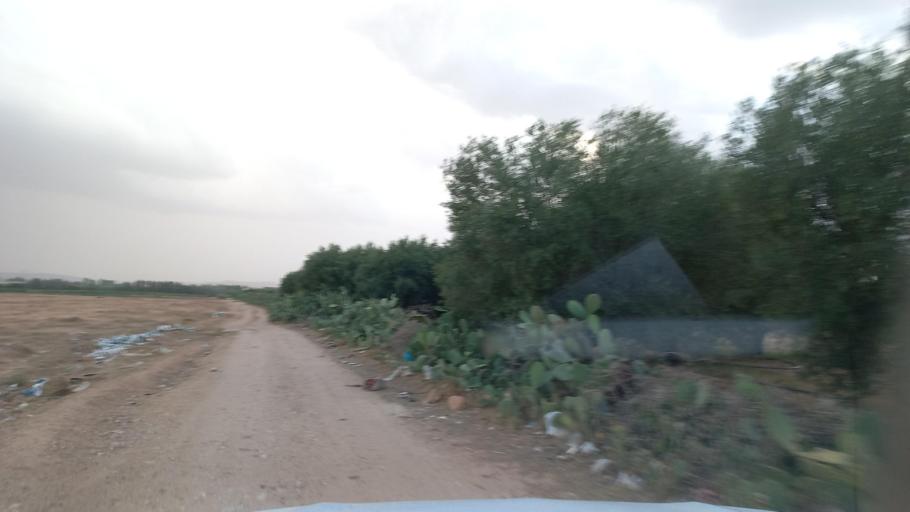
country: TN
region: Al Qasrayn
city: Kasserine
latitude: 35.2780
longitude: 9.0596
